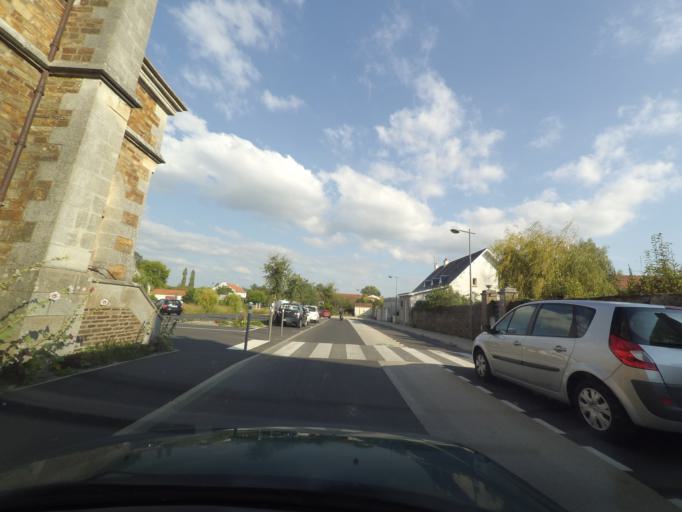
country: FR
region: Pays de la Loire
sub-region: Departement de la Loire-Atlantique
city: Saint-Philbert-de-Grand-Lieu
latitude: 47.0360
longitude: -1.6411
